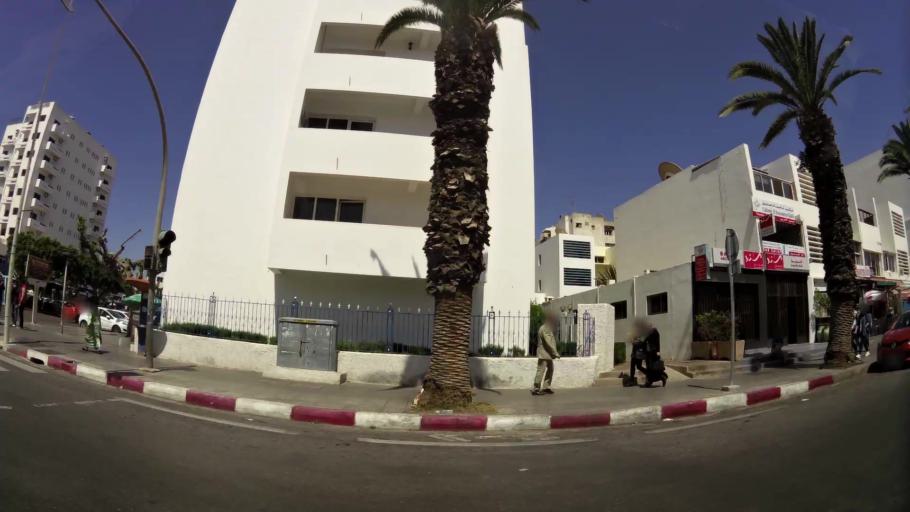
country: MA
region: Souss-Massa-Draa
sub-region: Agadir-Ida-ou-Tnan
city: Agadir
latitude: 30.4169
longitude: -9.5959
